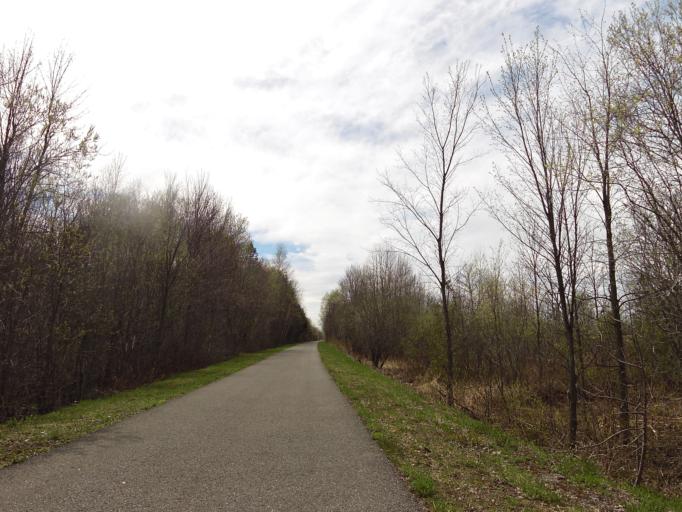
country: CA
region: Ontario
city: Hawkesbury
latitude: 45.5333
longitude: -74.6552
